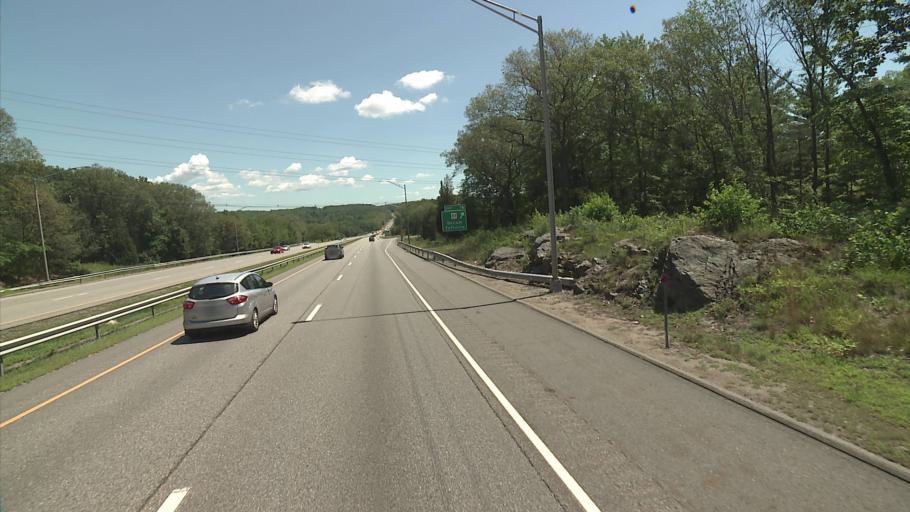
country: US
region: Connecticut
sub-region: New London County
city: Baltic
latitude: 41.5846
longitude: -72.0542
